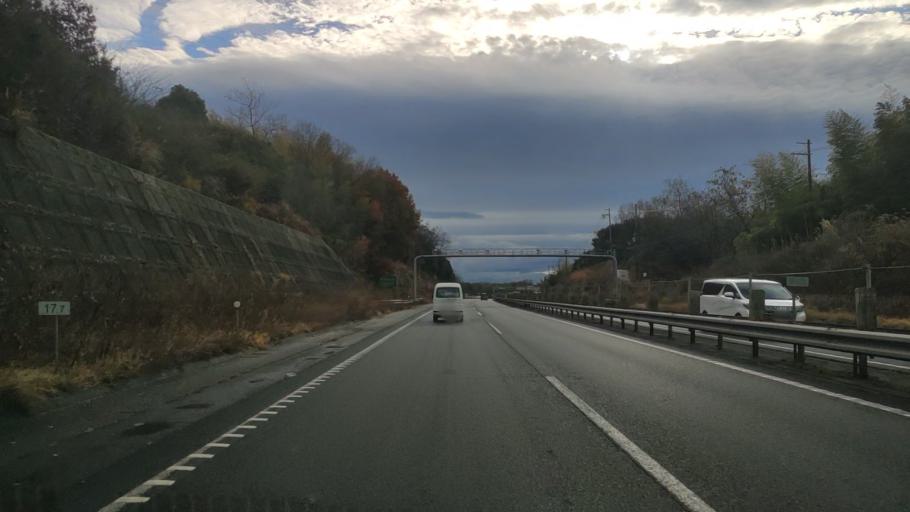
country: JP
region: Hyogo
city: Akashi
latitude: 34.7013
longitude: 134.9619
